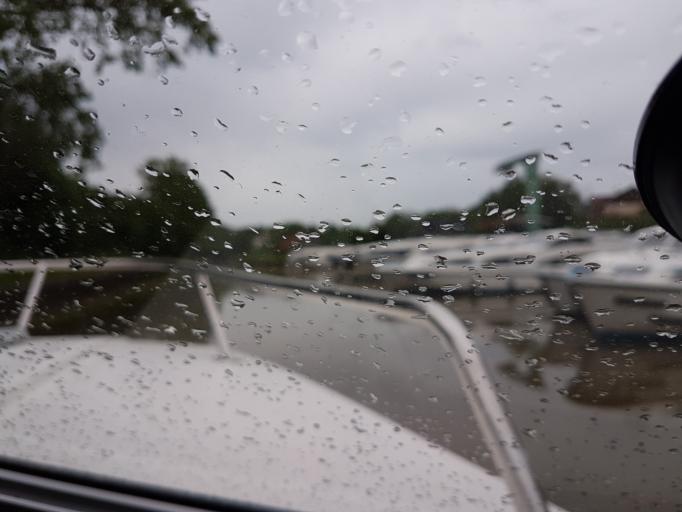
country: FR
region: Bourgogne
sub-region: Departement de la Nievre
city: Corbigny
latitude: 47.3616
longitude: 3.6193
